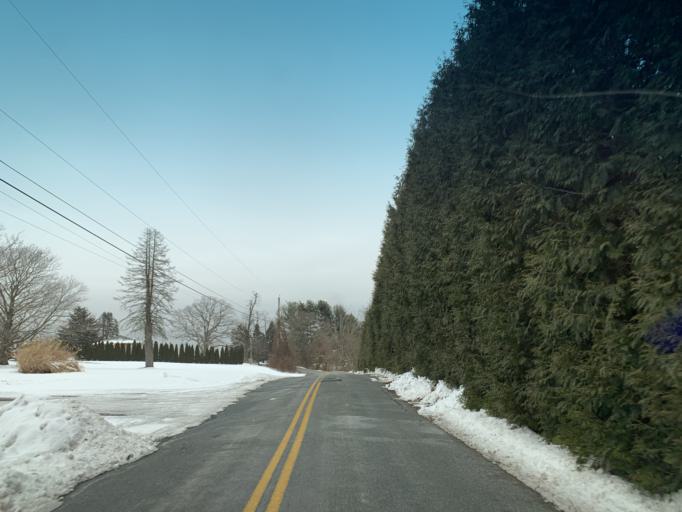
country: US
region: Maryland
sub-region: Harford County
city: Aberdeen
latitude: 39.5580
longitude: -76.1739
